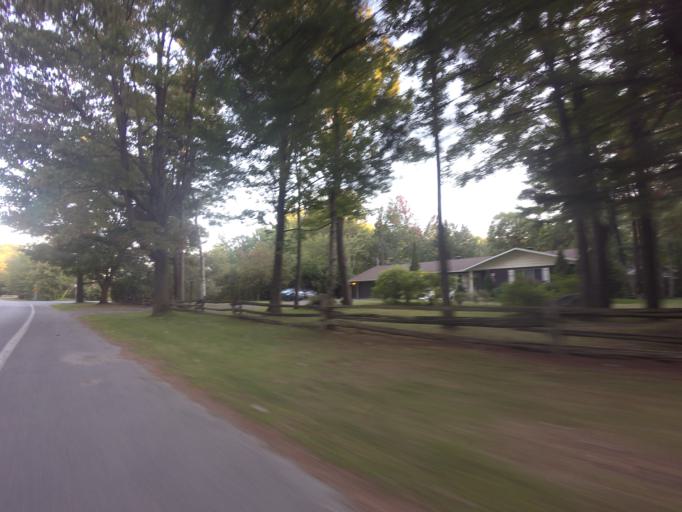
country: CA
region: Quebec
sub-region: Monteregie
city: Hudson
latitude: 45.4536
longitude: -74.1338
